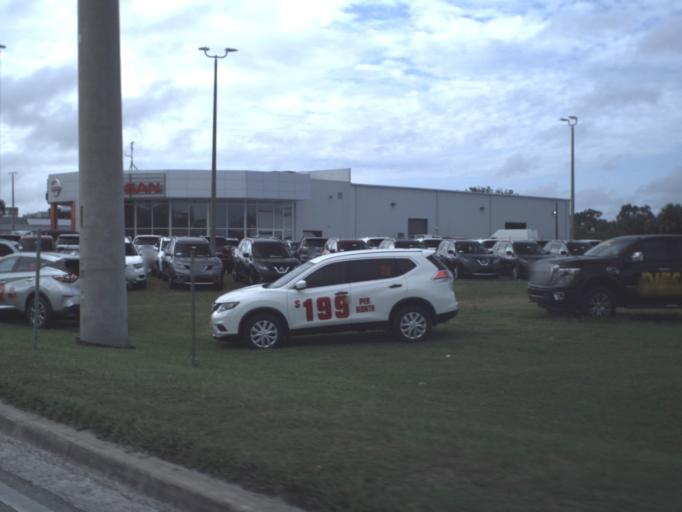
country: US
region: Florida
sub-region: Sarasota County
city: Venice
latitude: 27.0918
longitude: -82.4332
